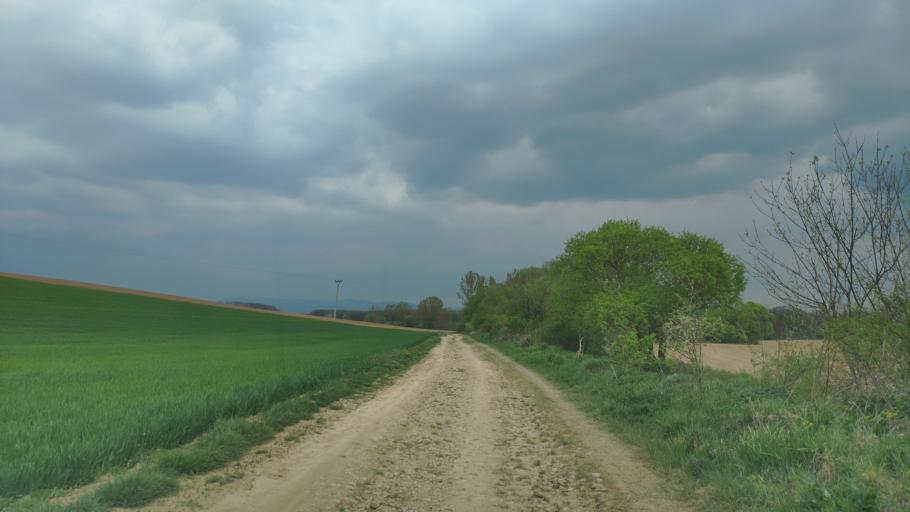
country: SK
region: Kosicky
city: Moldava nad Bodvou
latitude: 48.6069
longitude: 21.0400
